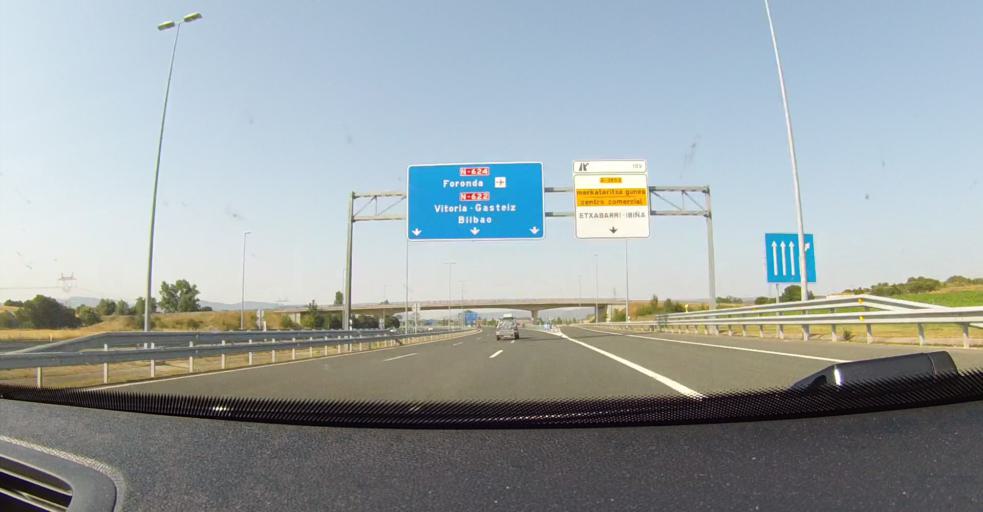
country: ES
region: Basque Country
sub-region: Provincia de Alava
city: Gasteiz / Vitoria
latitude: 42.9145
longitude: -2.6988
